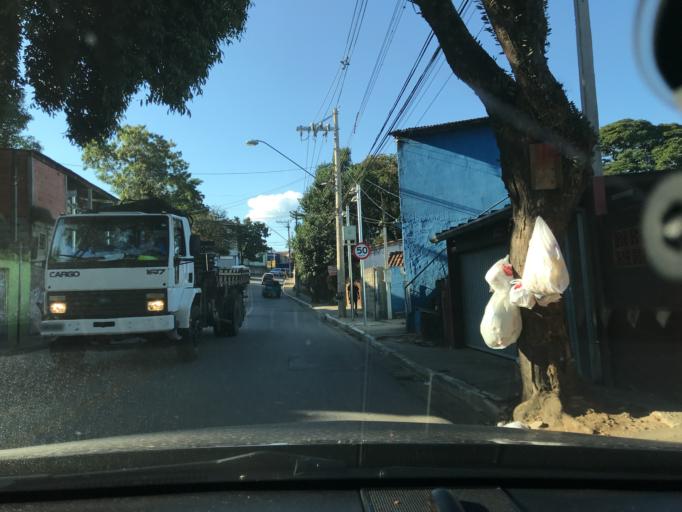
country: BR
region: Sao Paulo
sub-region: Sao Jose Dos Campos
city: Sao Jose dos Campos
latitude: -23.1579
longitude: -45.9031
